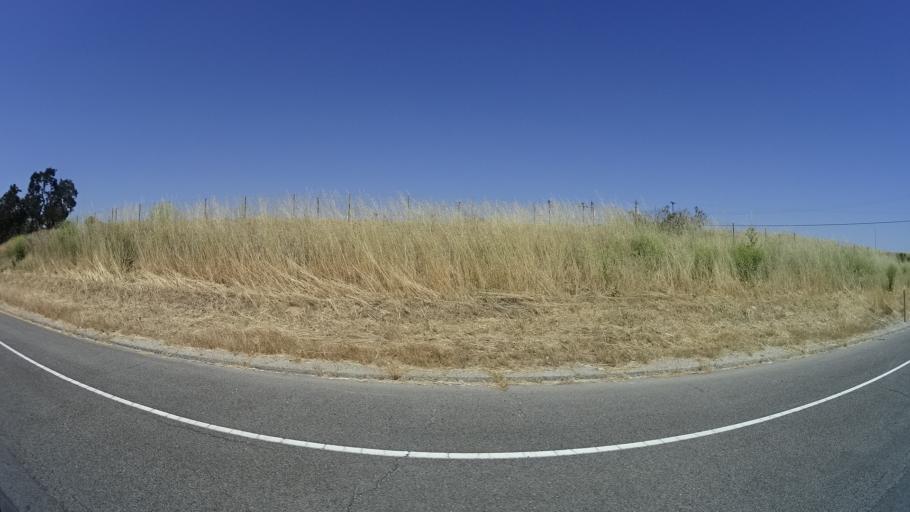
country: US
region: California
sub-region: San Luis Obispo County
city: San Miguel
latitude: 35.8166
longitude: -120.7552
